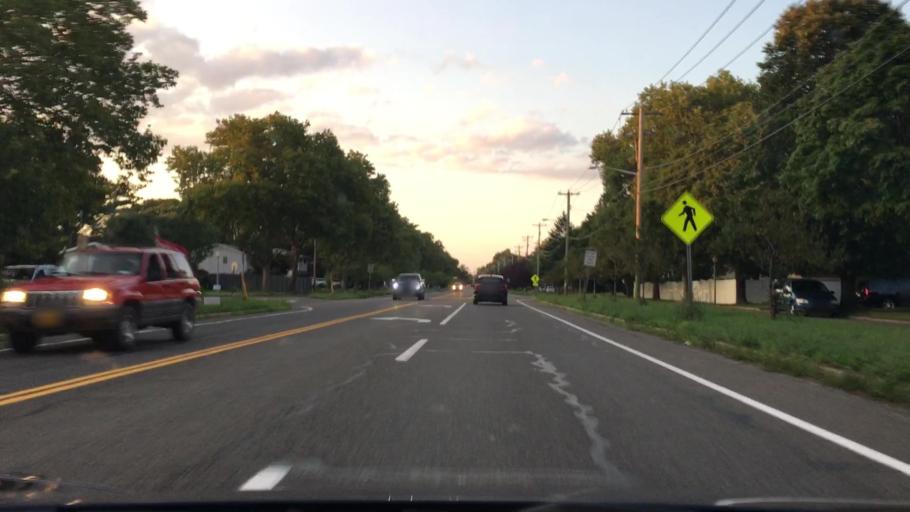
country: US
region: New York
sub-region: Suffolk County
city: Dix Hills
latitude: 40.7982
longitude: -73.2965
